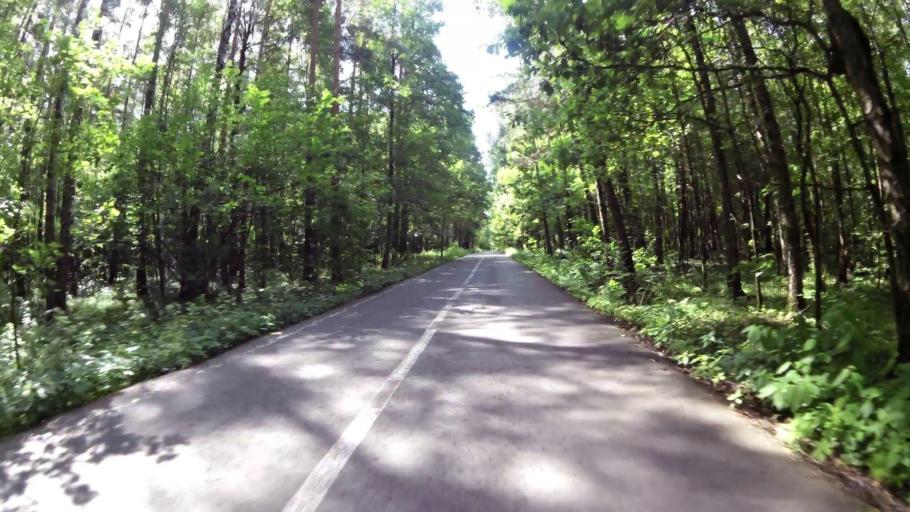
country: RU
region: Moscow
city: Babushkin
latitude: 55.8659
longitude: 37.7238
